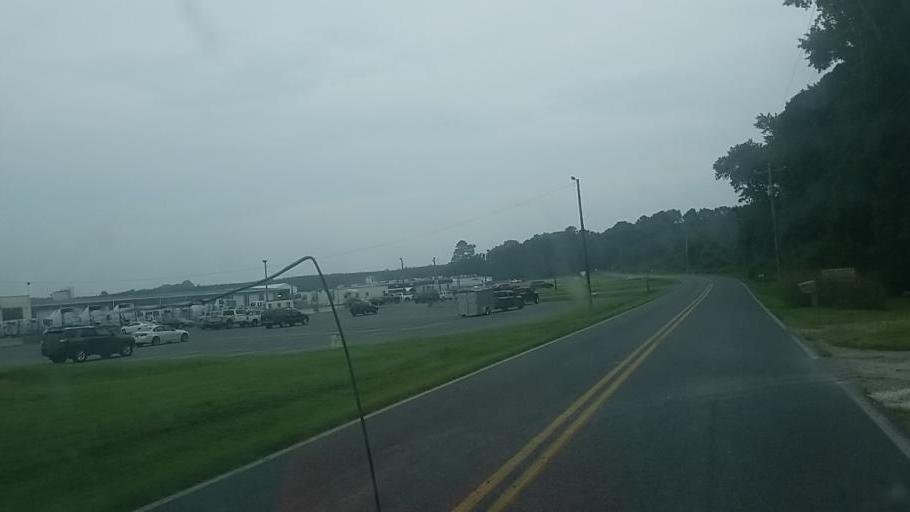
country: US
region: Maryland
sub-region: Wicomico County
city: Salisbury
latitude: 38.3833
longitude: -75.5264
